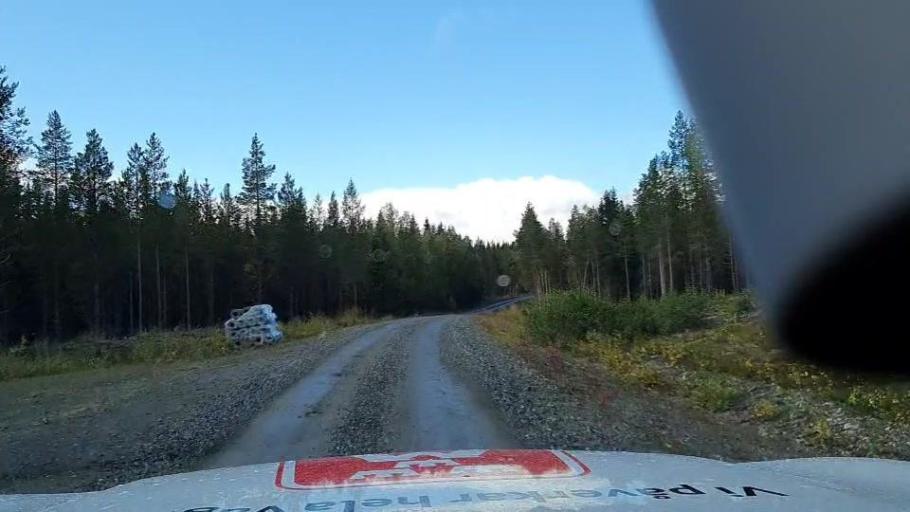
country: SE
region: Jaemtland
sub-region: Are Kommun
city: Are
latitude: 63.1877
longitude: 13.2006
